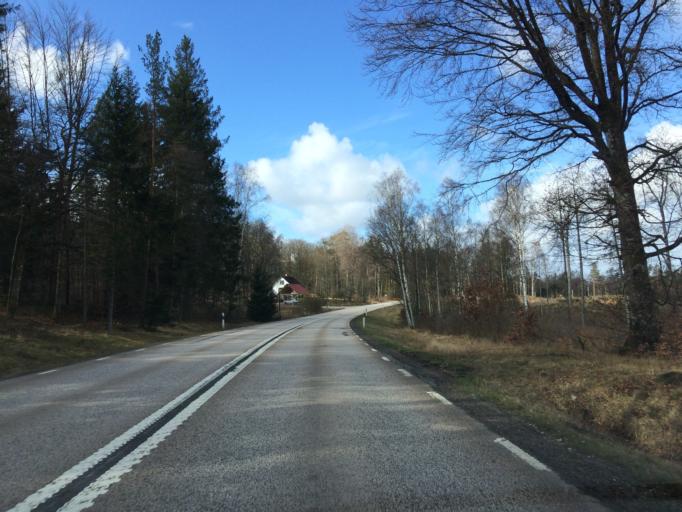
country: SE
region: Kronoberg
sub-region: Markaryds Kommun
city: Markaryd
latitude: 56.4766
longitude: 13.4915
